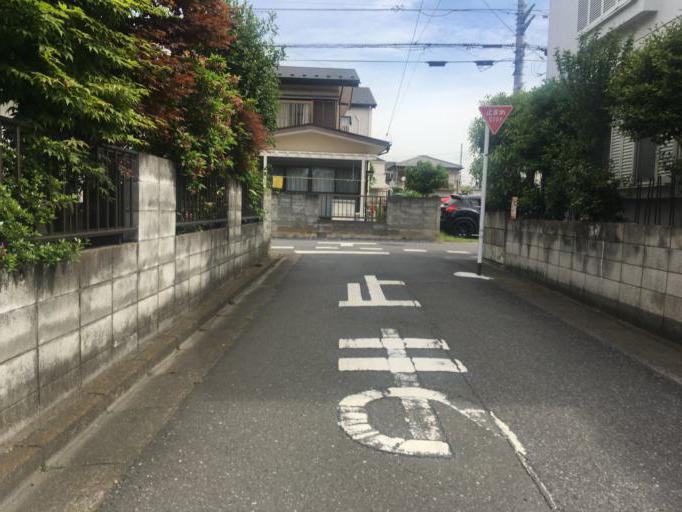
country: JP
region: Saitama
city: Yono
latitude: 35.8634
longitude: 139.6132
